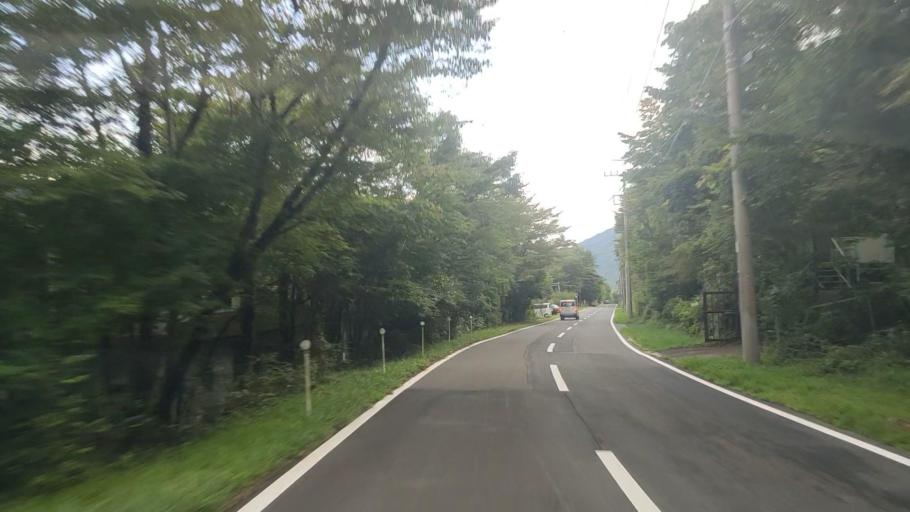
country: JP
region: Shizuoka
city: Gotemba
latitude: 35.2688
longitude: 138.8025
